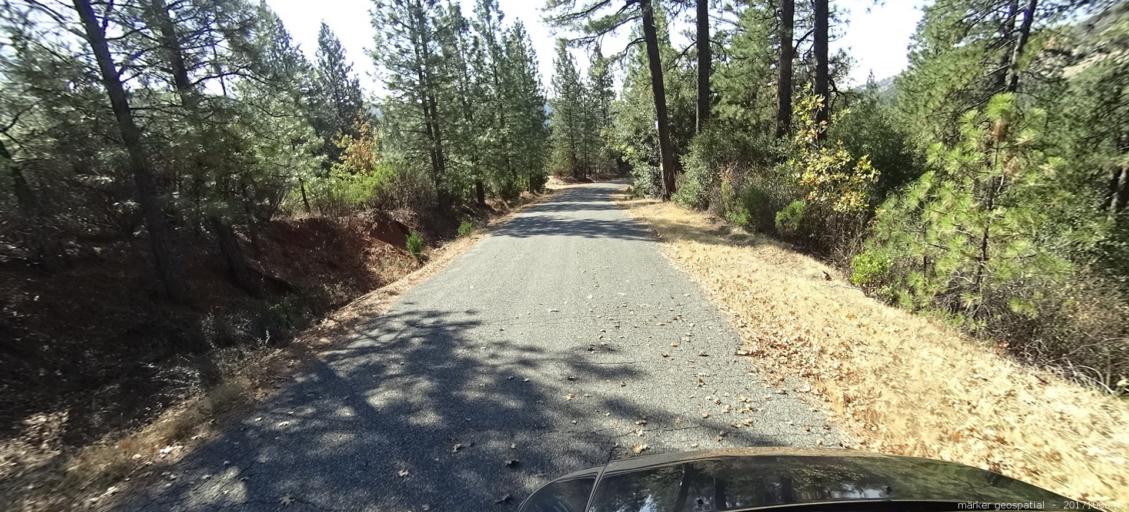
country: US
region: California
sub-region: Shasta County
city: Shingletown
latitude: 40.5774
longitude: -121.8781
